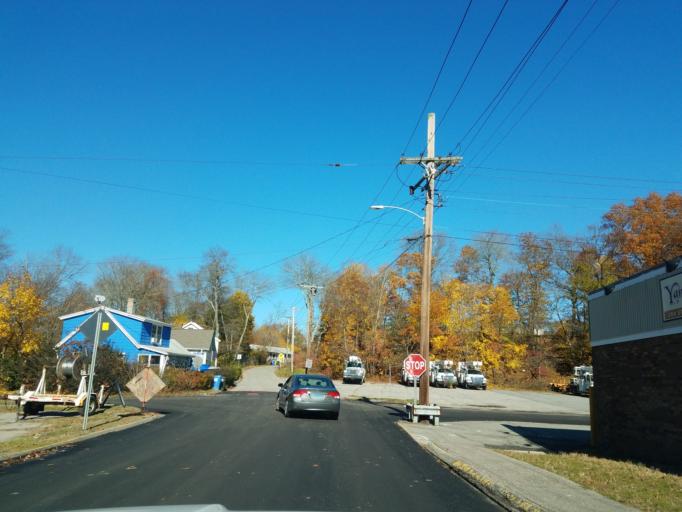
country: US
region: Connecticut
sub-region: New London County
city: Norwich
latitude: 41.5481
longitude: -72.1031
